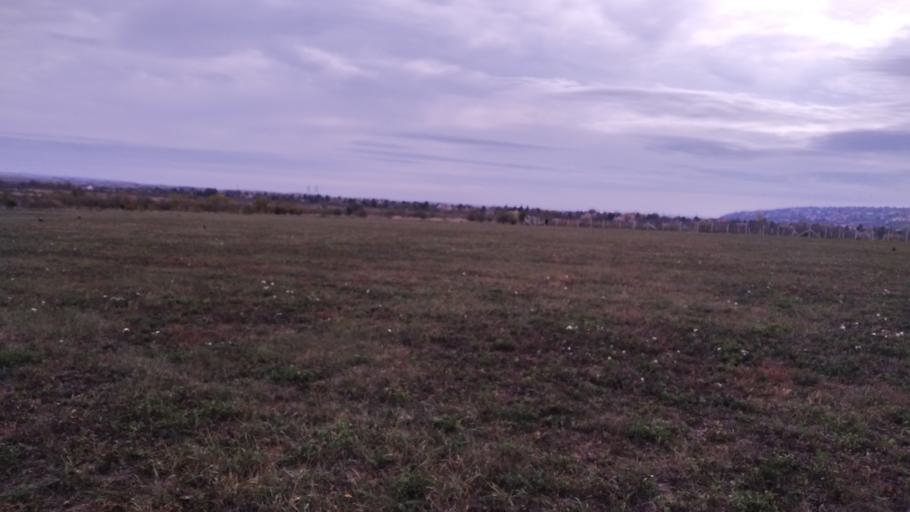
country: HU
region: Pest
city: Pomaz
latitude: 47.6405
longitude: 19.0462
